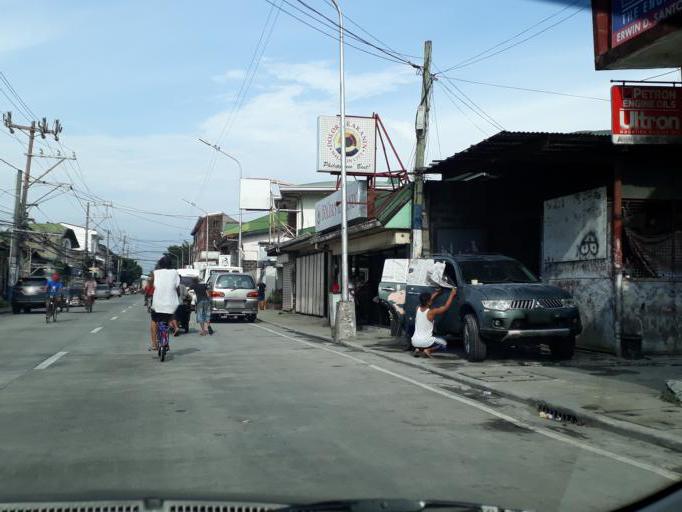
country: PH
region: Calabarzon
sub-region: Province of Rizal
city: Navotas
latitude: 14.6700
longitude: 120.9479
